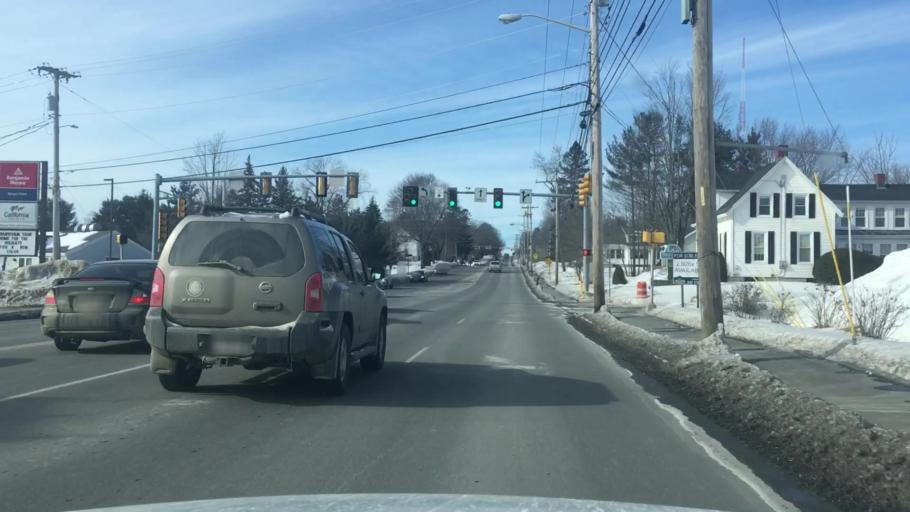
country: US
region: Maine
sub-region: Penobscot County
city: Bangor
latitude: 44.8254
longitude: -68.7811
